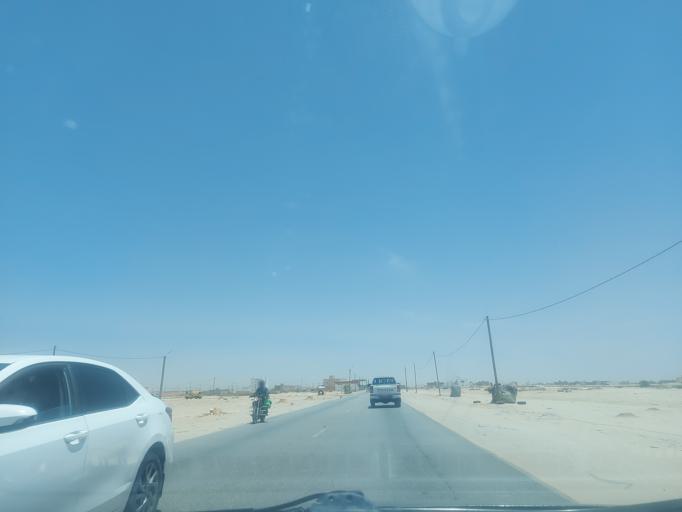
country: MR
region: Nouakchott
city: Nouakchott
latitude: 18.0794
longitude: -15.9546
